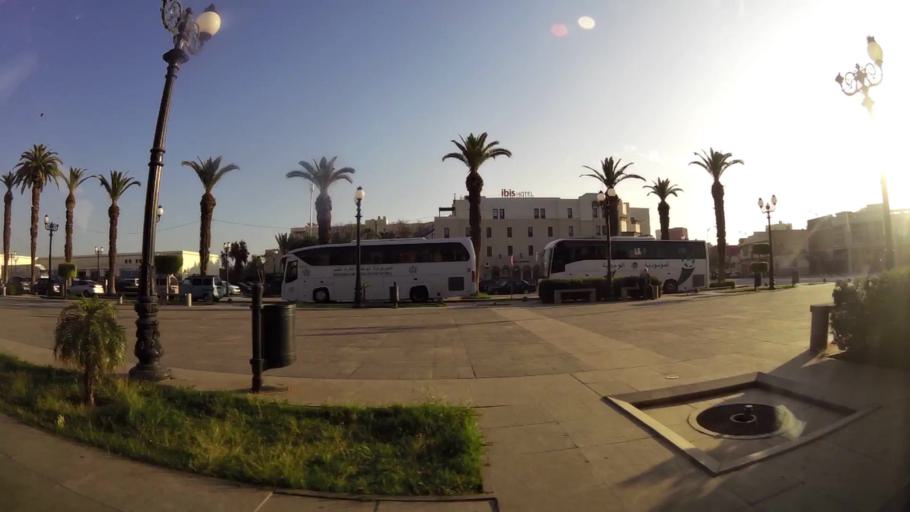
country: MA
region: Oriental
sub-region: Oujda-Angad
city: Oujda
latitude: 34.6811
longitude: -1.9227
